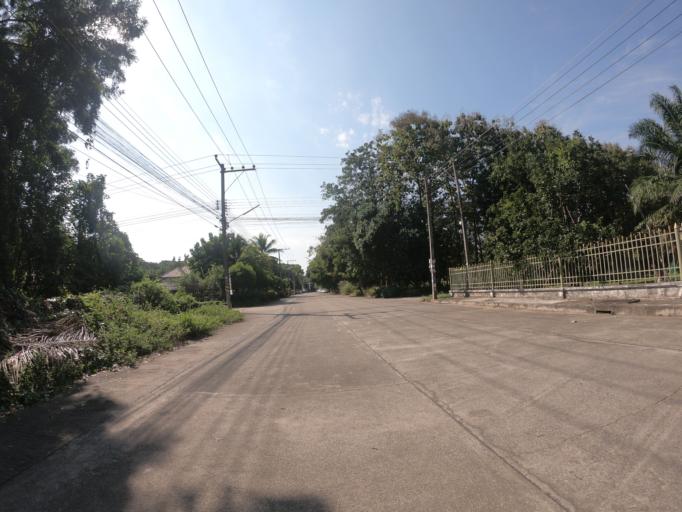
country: TH
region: Chiang Mai
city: Chiang Mai
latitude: 18.8041
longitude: 99.0074
